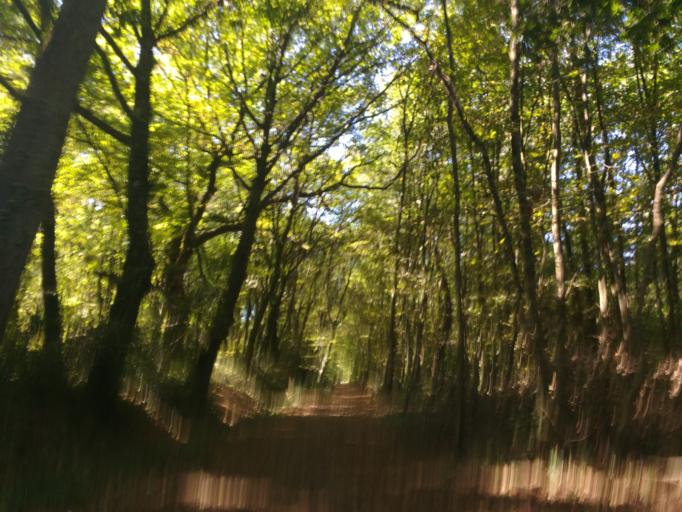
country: FR
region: Aquitaine
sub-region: Departement de la Gironde
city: Gradignan
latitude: 44.7891
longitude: -0.6148
